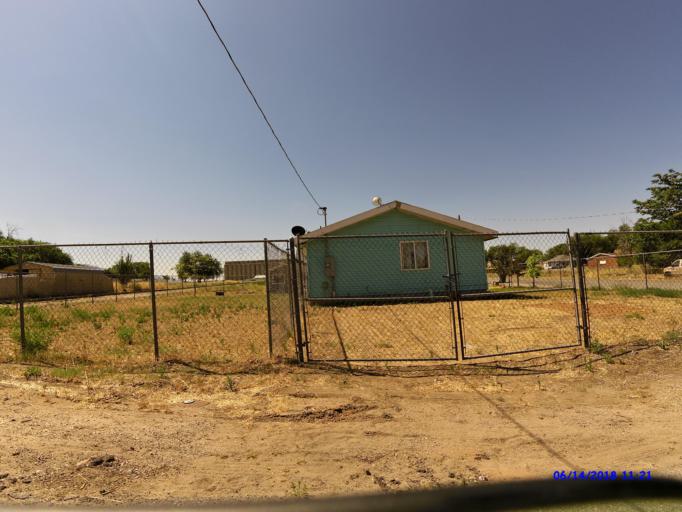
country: US
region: Utah
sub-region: Weber County
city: Ogden
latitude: 41.2195
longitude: -111.9988
